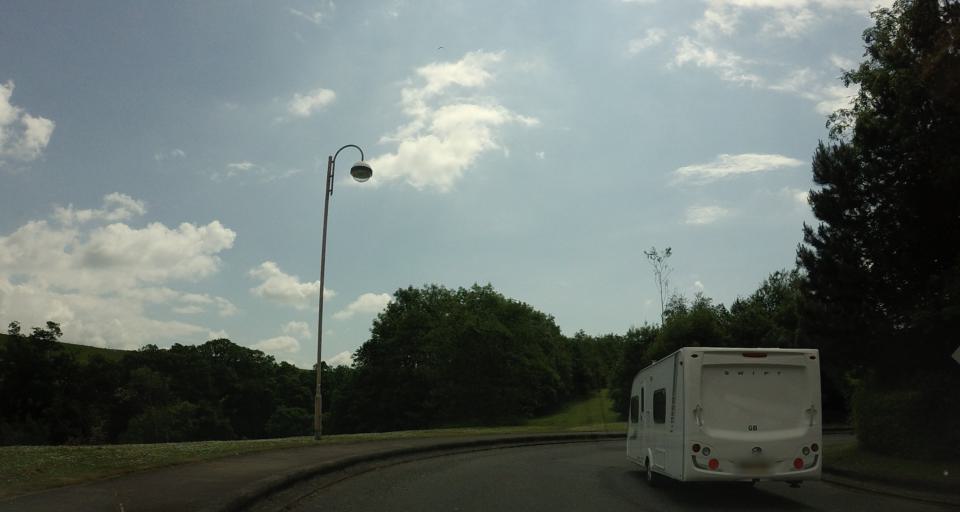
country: GB
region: Scotland
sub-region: Dumfries and Galloway
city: Lochmaben
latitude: 55.2183
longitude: -3.4096
